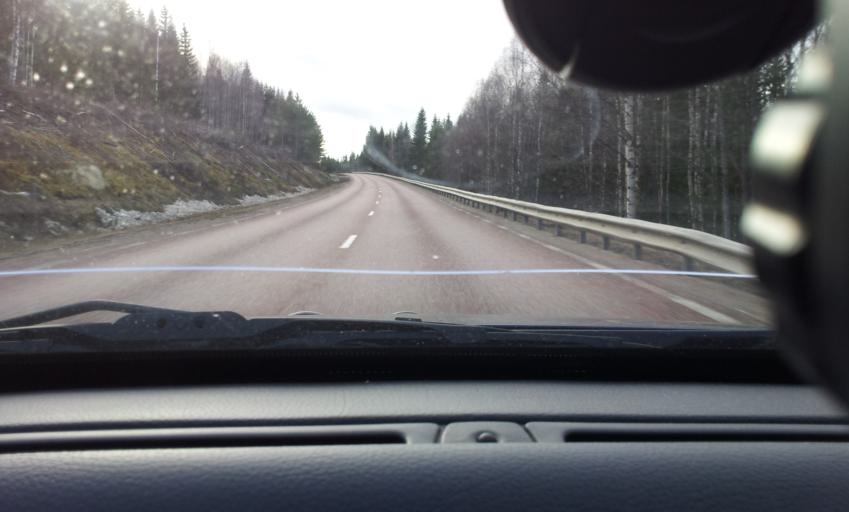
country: SE
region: Gaevleborg
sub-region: Ljusdals Kommun
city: Farila
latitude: 61.8866
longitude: 15.6986
